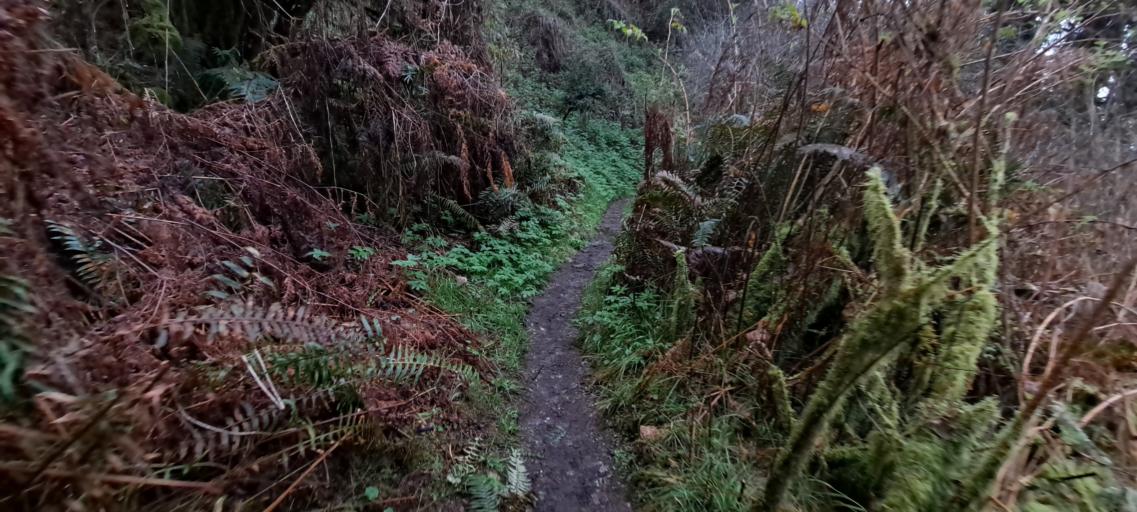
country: US
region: California
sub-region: Humboldt County
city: Ferndale
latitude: 40.5706
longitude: -124.2583
